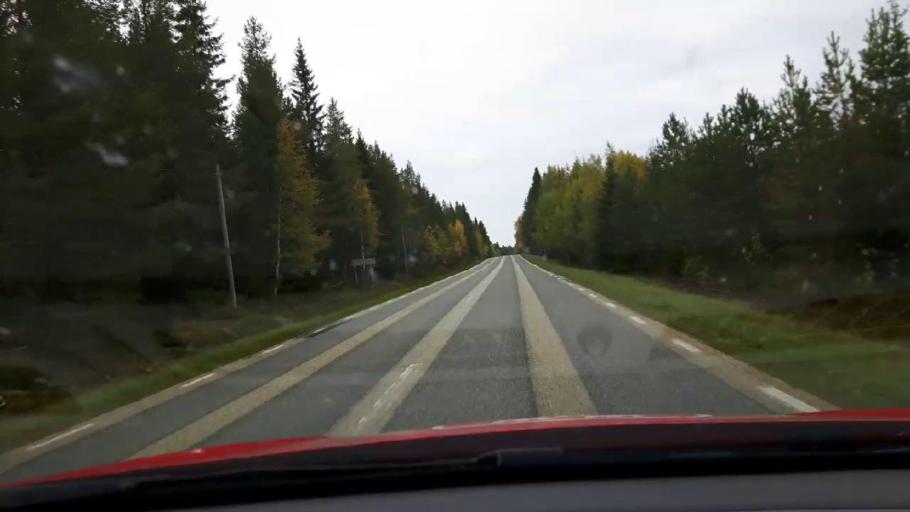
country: SE
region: Jaemtland
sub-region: Bergs Kommun
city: Hoverberg
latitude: 62.8975
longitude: 14.3464
